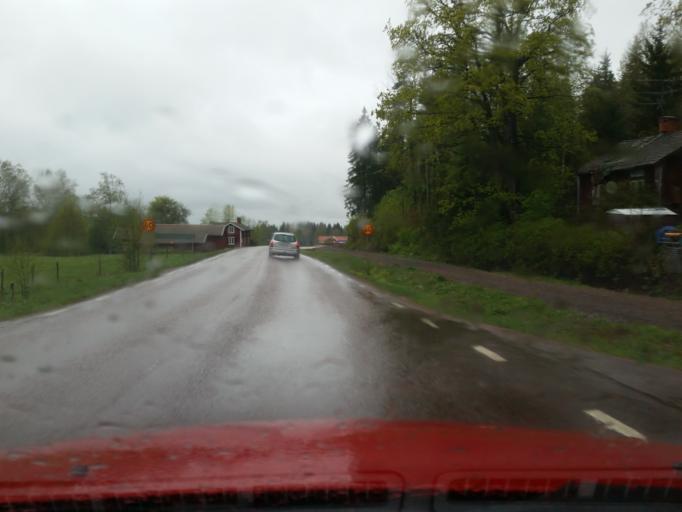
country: SE
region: Dalarna
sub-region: Saters Kommun
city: Saeter
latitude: 60.3475
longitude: 15.7828
